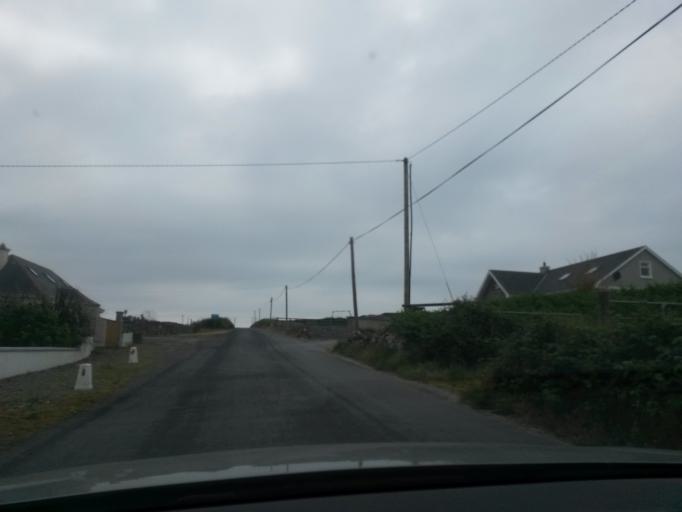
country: IE
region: Munster
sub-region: Ciarrai
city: Ballybunnion
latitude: 52.6767
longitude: -9.6650
